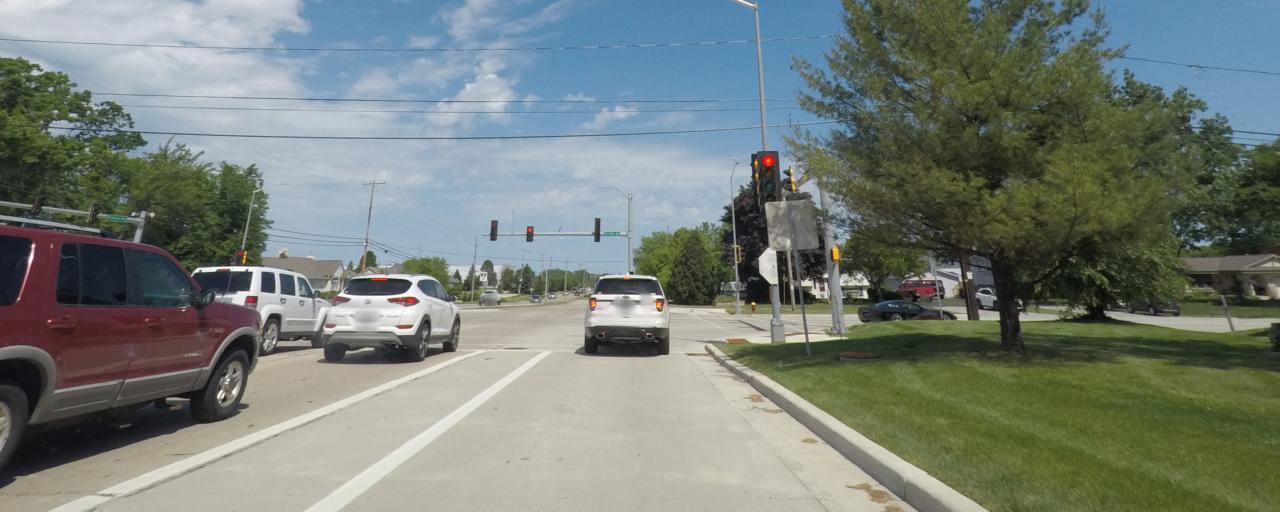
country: US
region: Wisconsin
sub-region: Milwaukee County
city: Oak Creek
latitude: 42.9015
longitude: -87.9319
